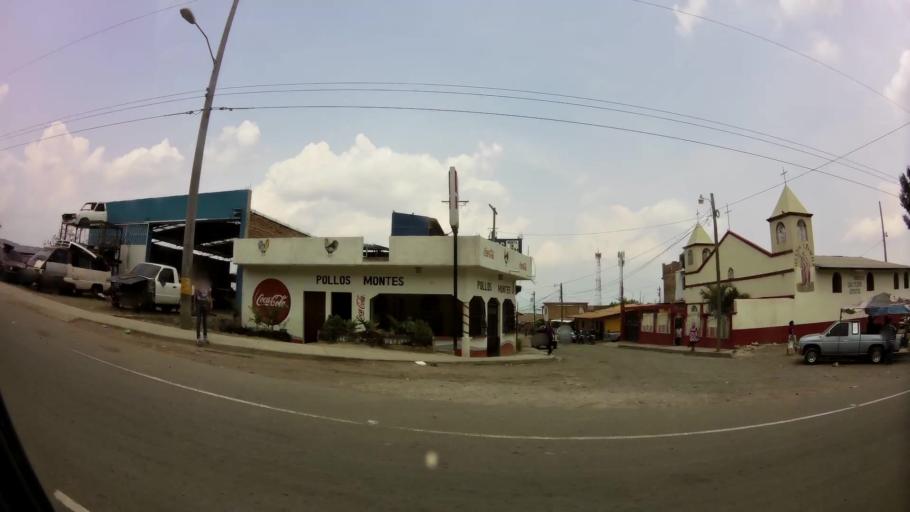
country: HN
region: Francisco Morazan
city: El Lolo
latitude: 14.1013
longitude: -87.2518
